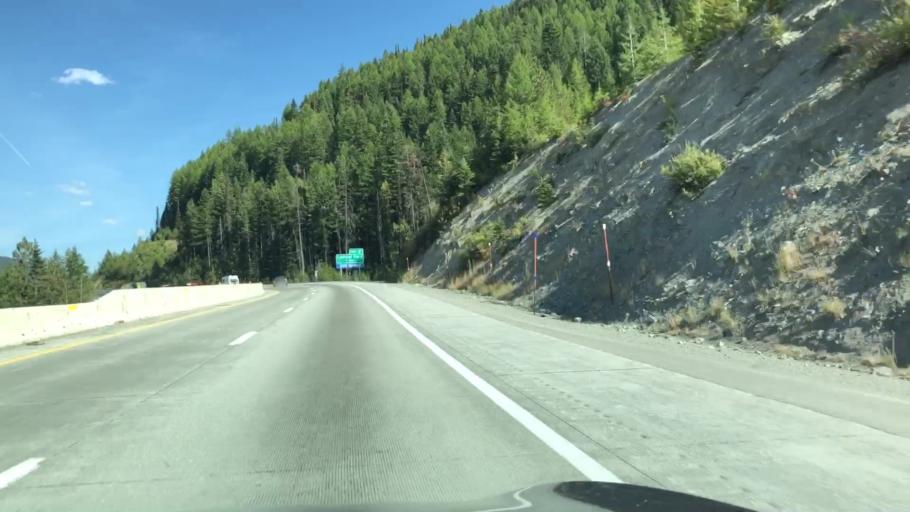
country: US
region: Idaho
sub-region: Shoshone County
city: Wallace
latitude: 47.4624
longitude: -115.7067
